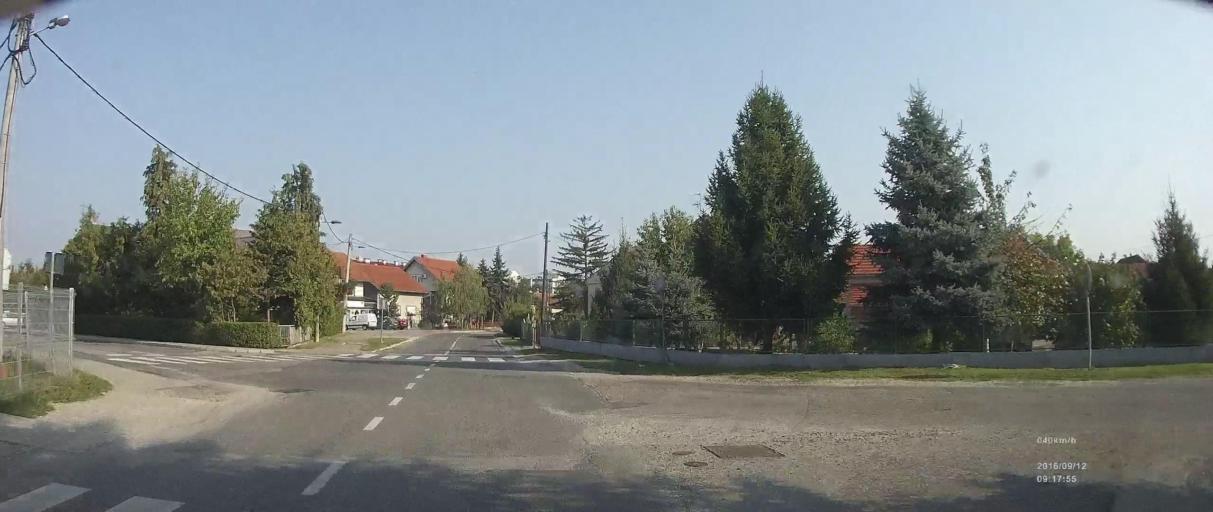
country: HR
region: Zagrebacka
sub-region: Grad Velika Gorica
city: Velika Gorica
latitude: 45.7064
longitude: 16.0695
